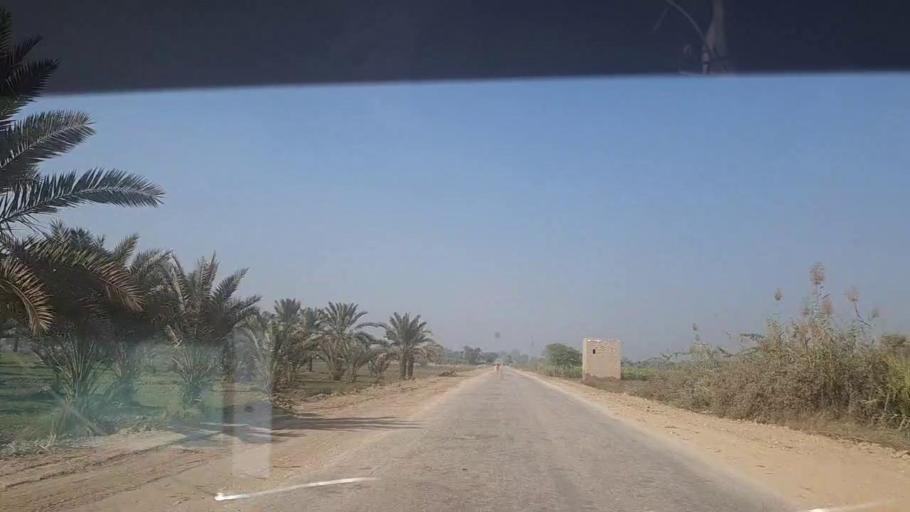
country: PK
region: Sindh
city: Kot Diji
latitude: 27.4239
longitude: 68.6581
